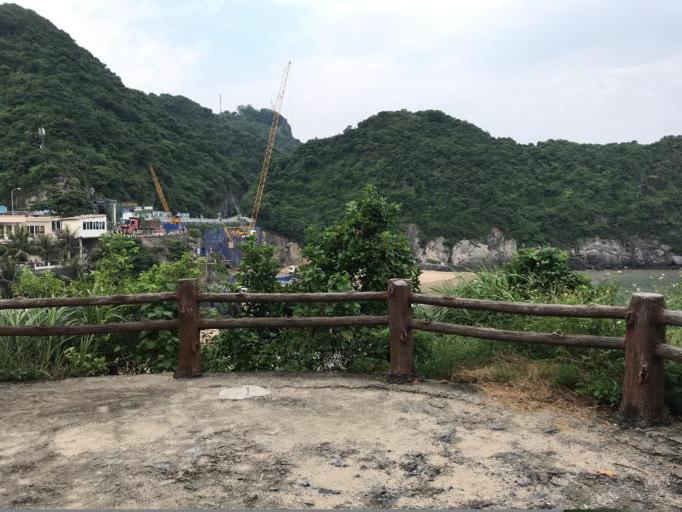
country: VN
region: Hai Phong
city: Cat Ba
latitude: 20.7169
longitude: 107.0522
